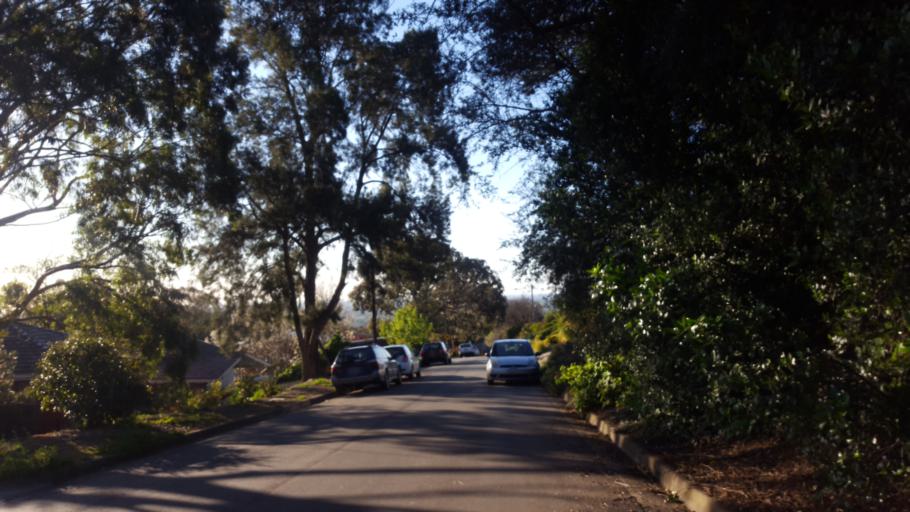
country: AU
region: South Australia
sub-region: Burnside
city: Beaumont
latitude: -34.9549
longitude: 138.6575
